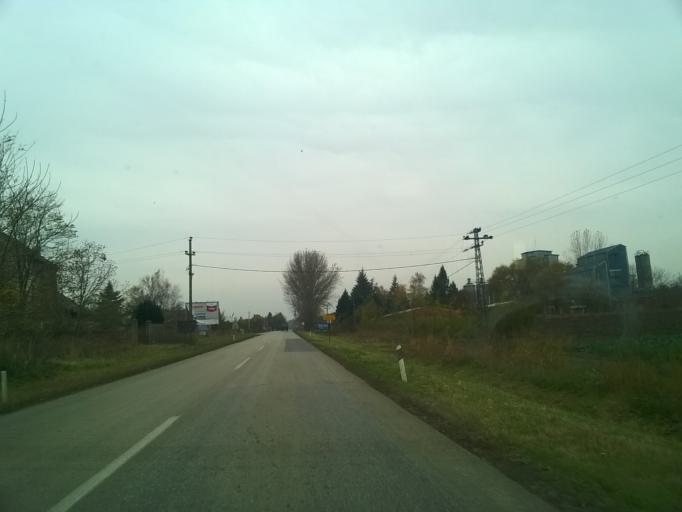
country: RS
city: Crepaja
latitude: 44.9991
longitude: 20.6402
